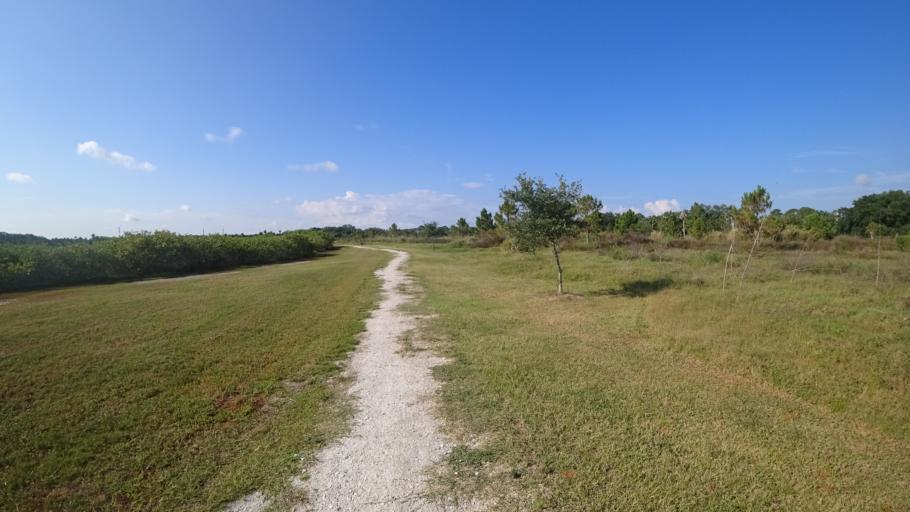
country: US
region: Florida
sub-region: Manatee County
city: Ellenton
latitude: 27.5014
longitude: -82.4896
